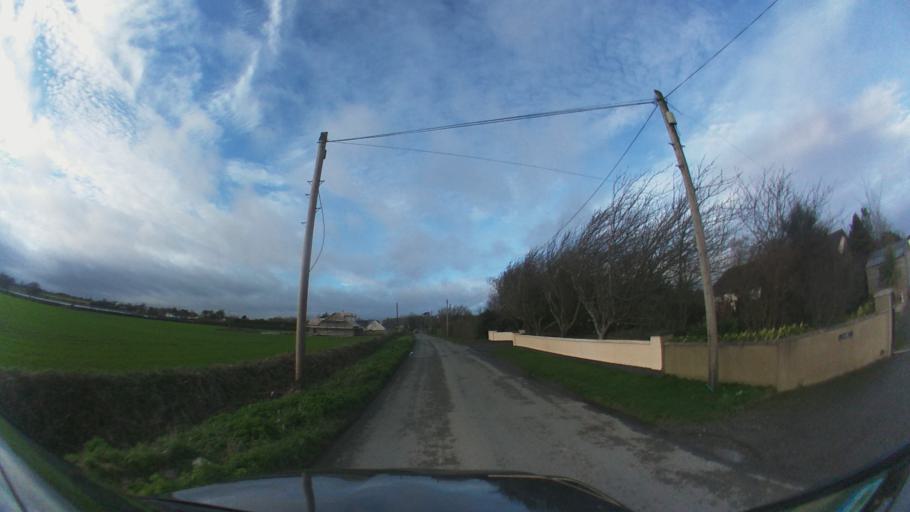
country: IE
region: Leinster
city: Balrothery
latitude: 53.5770
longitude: -6.1573
